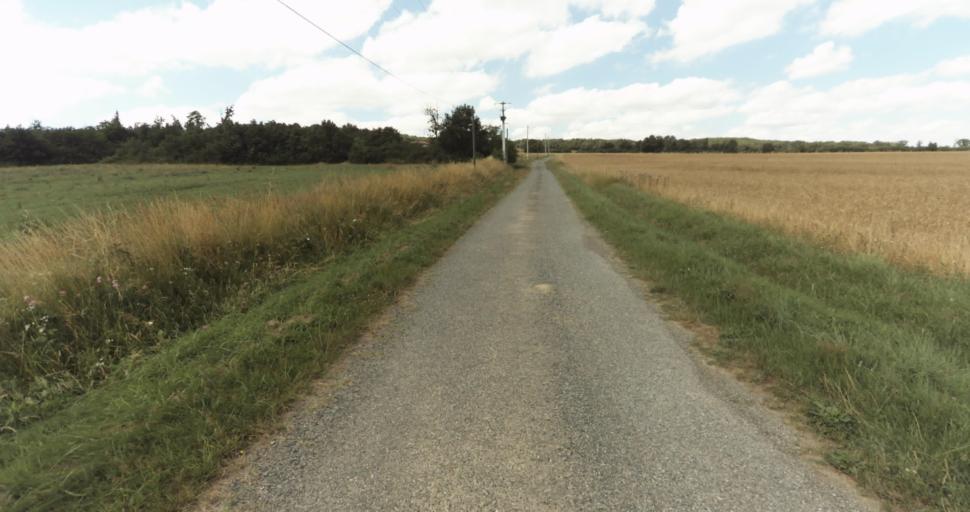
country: FR
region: Midi-Pyrenees
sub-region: Departement de la Haute-Garonne
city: Fontenilles
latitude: 43.5685
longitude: 1.1697
